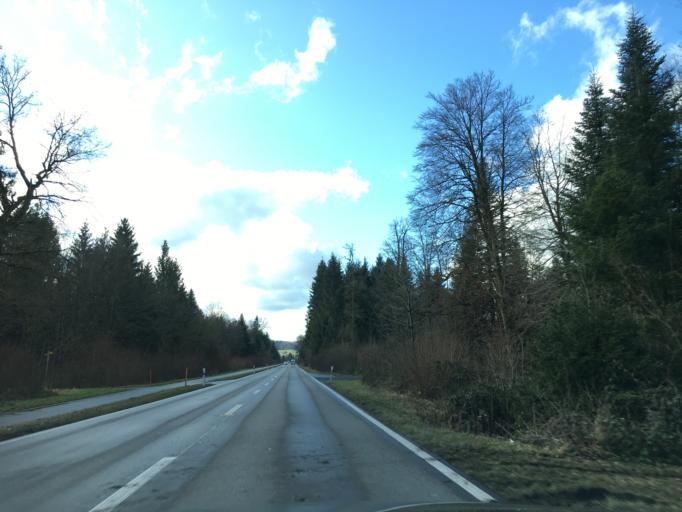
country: CH
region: Zug
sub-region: Zug
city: Hunenberg
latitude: 47.1968
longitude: 8.4235
